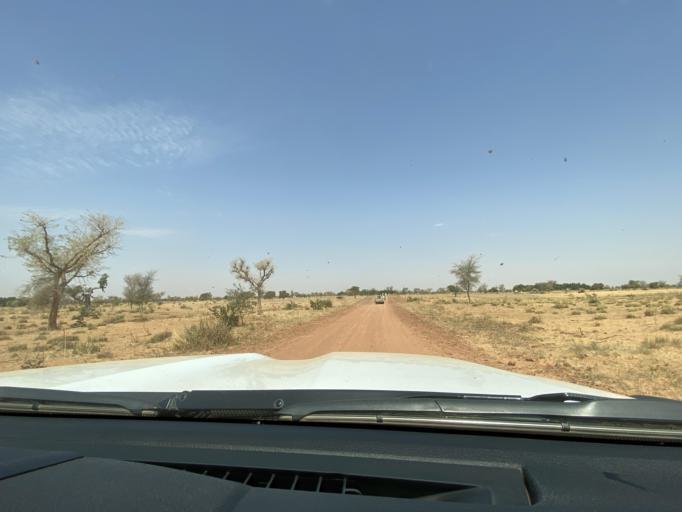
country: NE
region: Dosso
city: Birnin Gaoure
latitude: 13.2364
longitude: 2.8676
